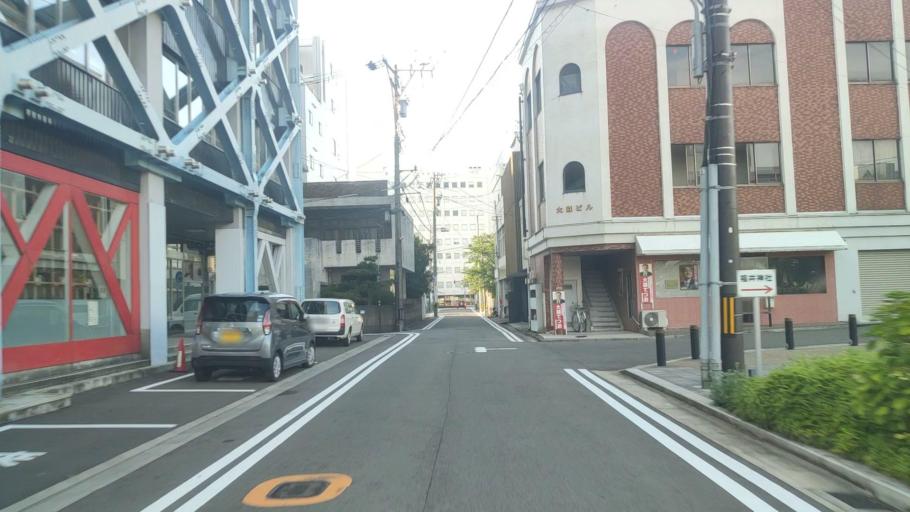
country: JP
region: Fukui
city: Fukui-shi
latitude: 36.0657
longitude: 136.2188
